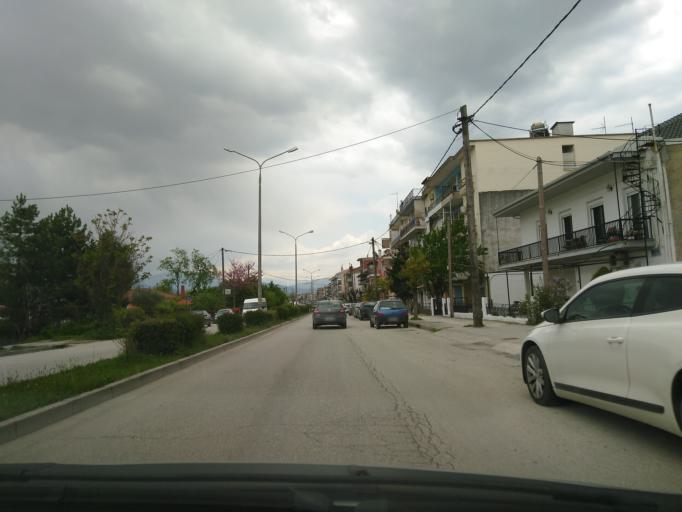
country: GR
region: Epirus
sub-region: Nomos Ioanninon
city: Ioannina
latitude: 39.6765
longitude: 20.8429
